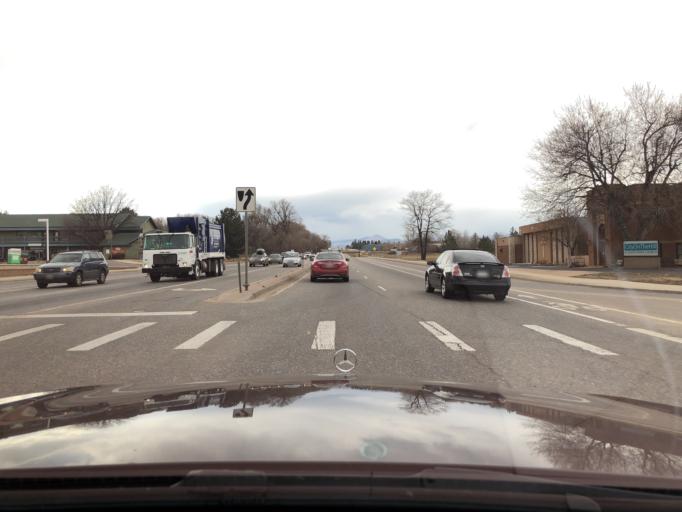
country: US
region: Colorado
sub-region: Boulder County
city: Gunbarrel
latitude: 40.0147
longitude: -105.1781
